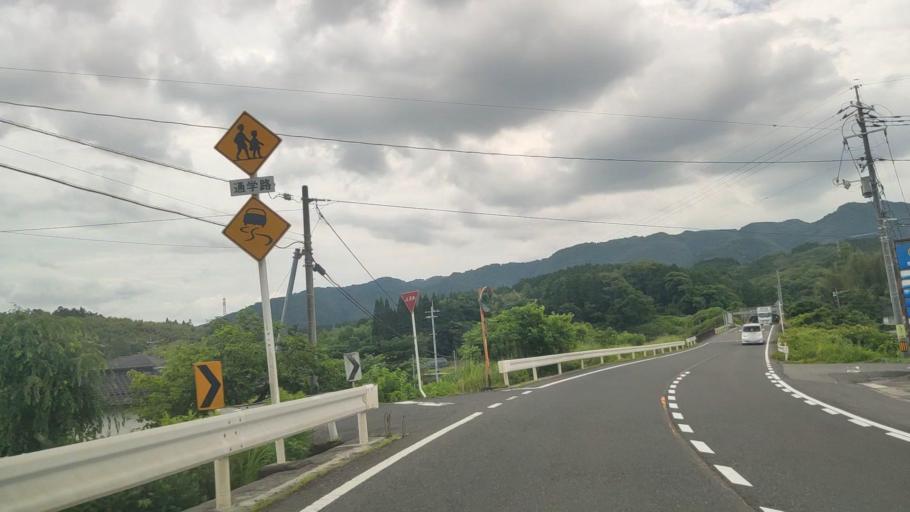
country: JP
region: Okayama
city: Tsuyama
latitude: 35.0647
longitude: 133.8562
